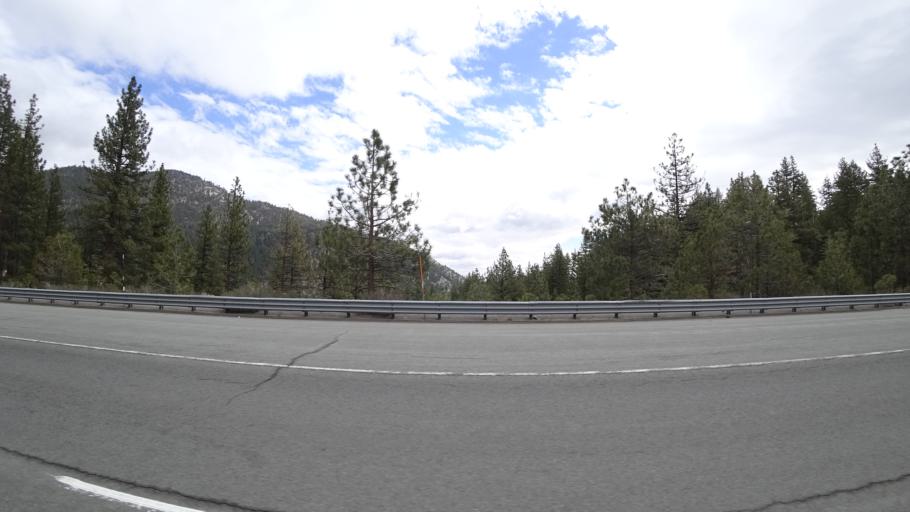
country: US
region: Nevada
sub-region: Douglas County
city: Indian Hills
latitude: 39.1094
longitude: -119.8790
